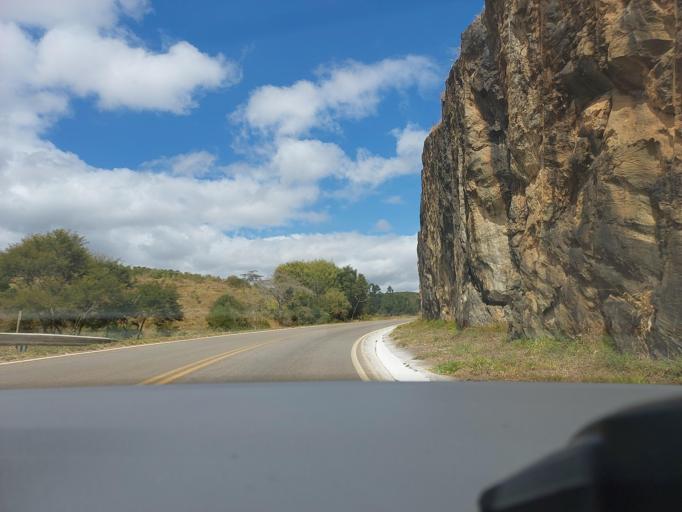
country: BR
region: Minas Gerais
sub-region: Visconde Do Rio Branco
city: Visconde do Rio Branco
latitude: -20.9396
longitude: -42.6270
